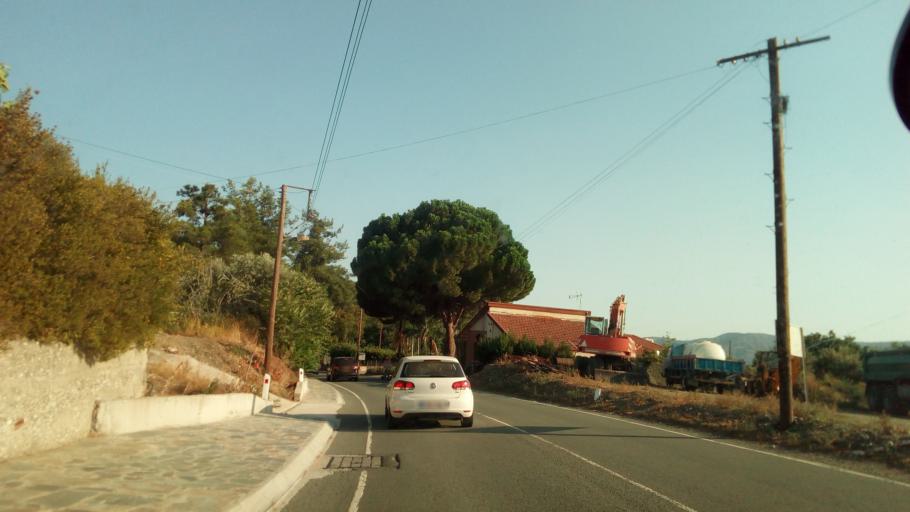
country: CY
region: Limassol
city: Pelendri
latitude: 34.8560
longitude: 32.9126
